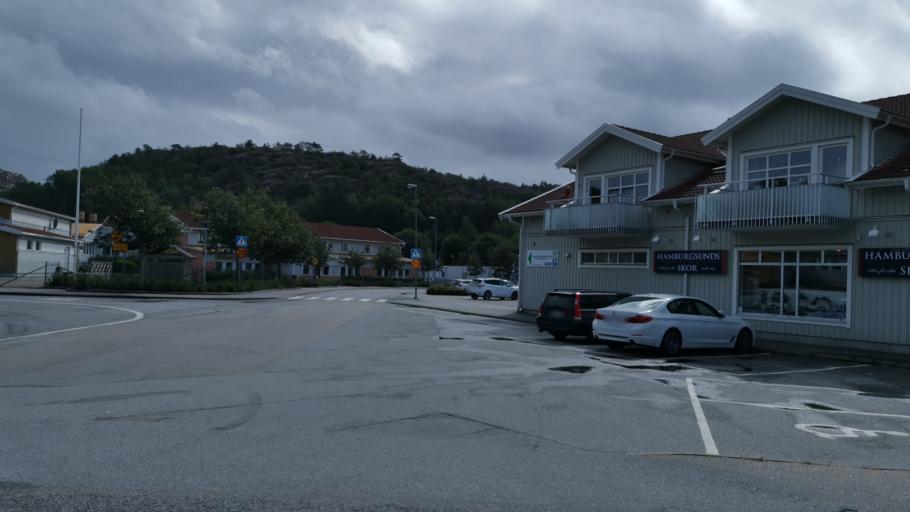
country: SE
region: Vaestra Goetaland
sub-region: Sotenas Kommun
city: Hunnebostrand
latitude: 58.5525
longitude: 11.2727
